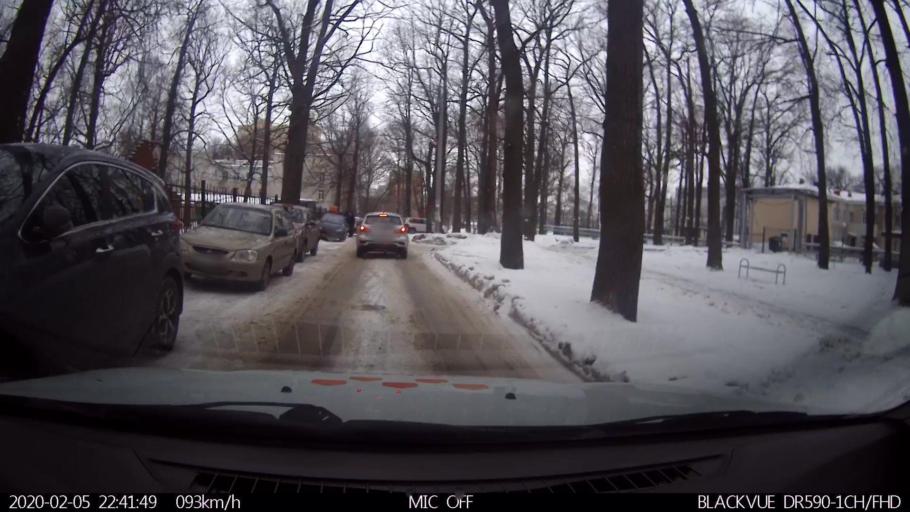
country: RU
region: Nizjnij Novgorod
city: Imeni Stepana Razina
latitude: 54.7198
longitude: 44.3453
